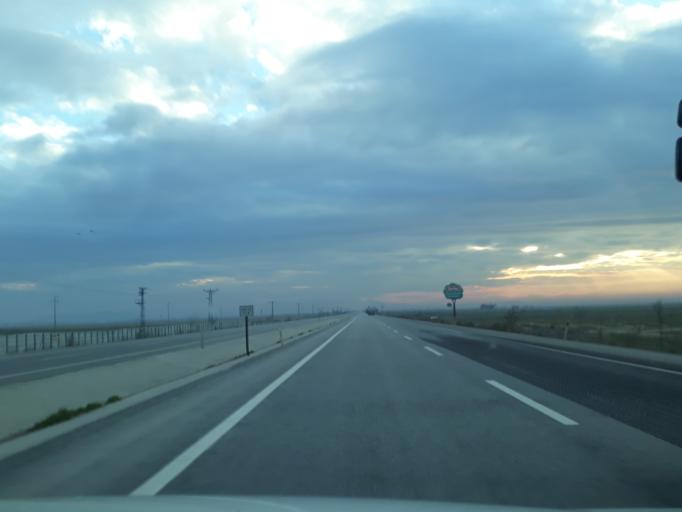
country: TR
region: Konya
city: Hotamis
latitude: 37.7107
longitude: 33.2837
